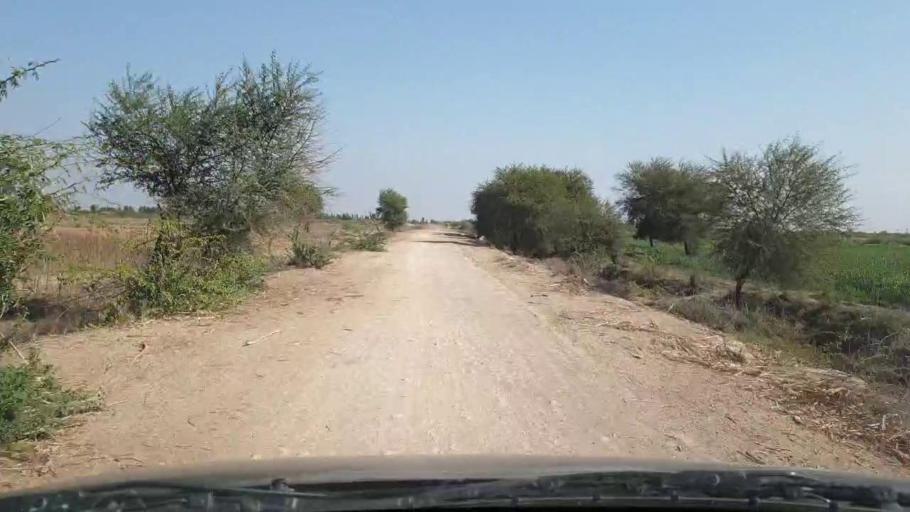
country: PK
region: Sindh
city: Samaro
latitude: 25.1970
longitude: 69.2729
